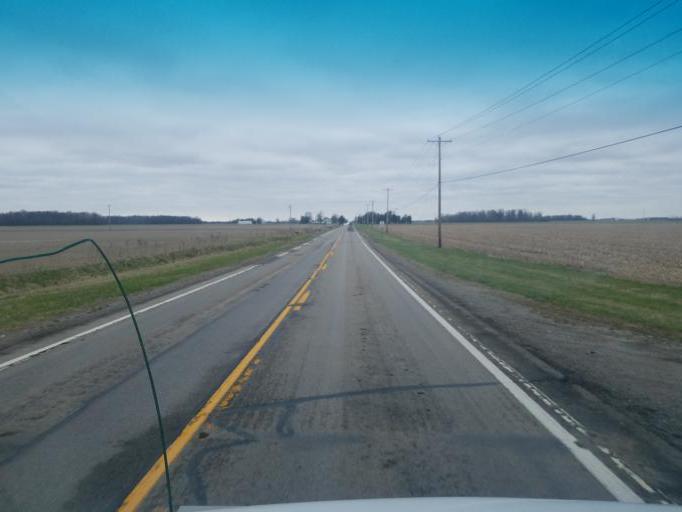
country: US
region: Ohio
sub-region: Allen County
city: Delphos
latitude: 40.8759
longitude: -84.3503
